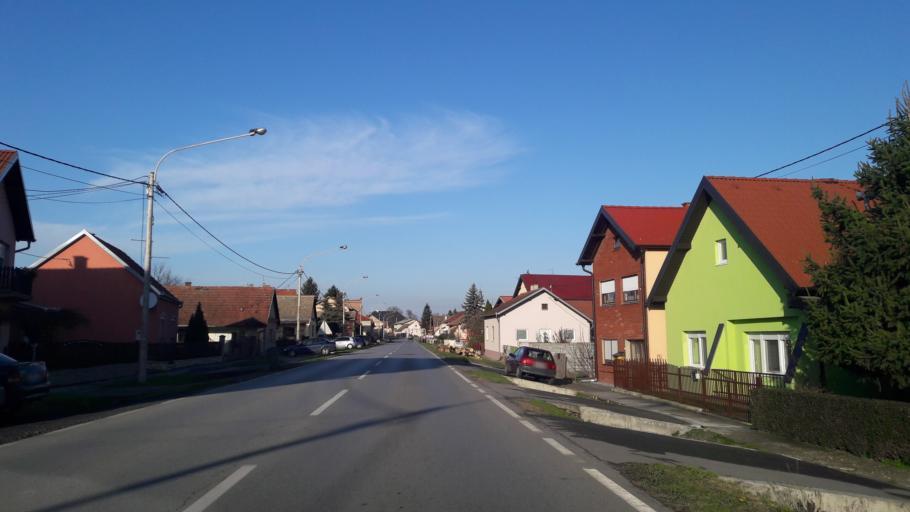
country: HR
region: Osjecko-Baranjska
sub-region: Grad Osijek
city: Bilje
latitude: 45.5996
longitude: 18.7430
